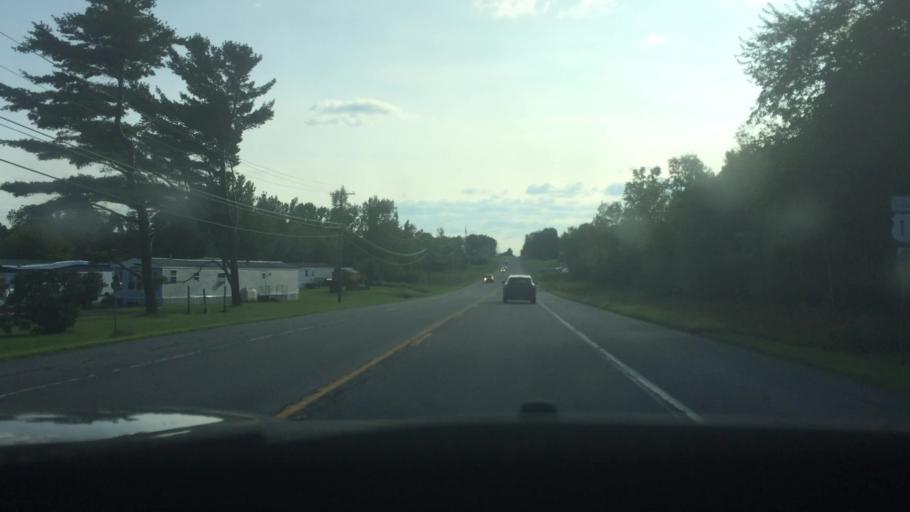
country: US
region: New York
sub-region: St. Lawrence County
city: Canton
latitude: 44.6112
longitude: -75.1190
